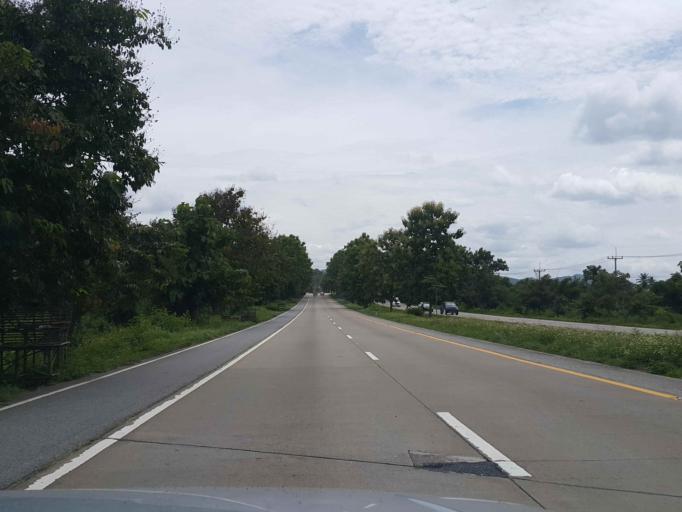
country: TH
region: Lamphun
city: Mae Tha
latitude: 18.4741
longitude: 99.1275
